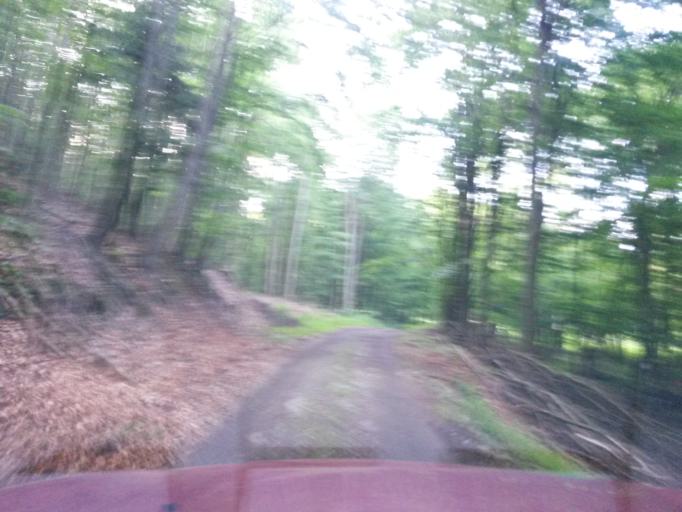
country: SK
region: Kosicky
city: Moldava nad Bodvou
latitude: 48.7384
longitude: 21.0638
